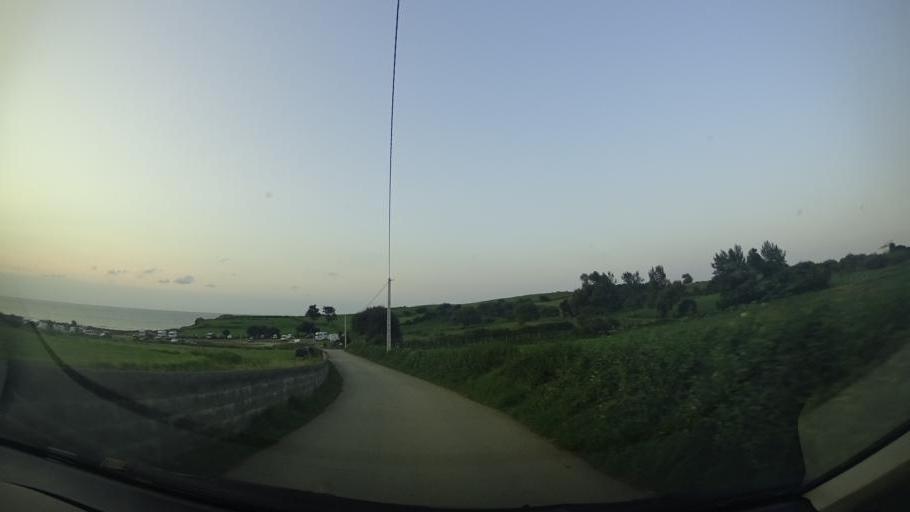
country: ES
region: Asturias
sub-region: Province of Asturias
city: Colunga
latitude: 43.4715
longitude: -5.2037
